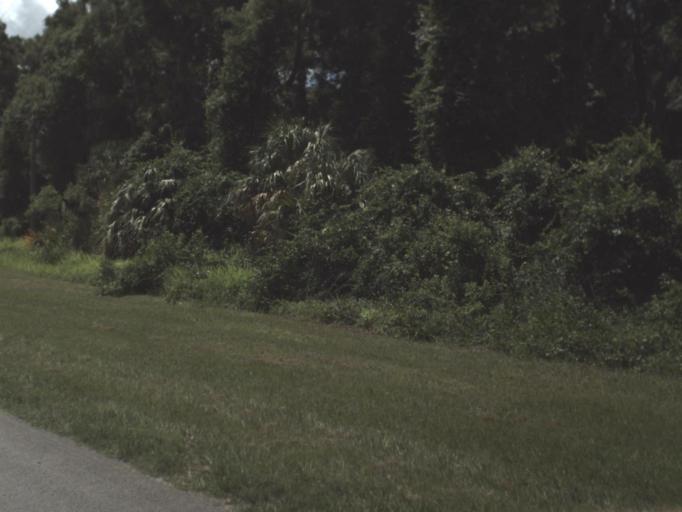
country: US
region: Florida
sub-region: Putnam County
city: Palatka
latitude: 29.5213
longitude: -81.6277
